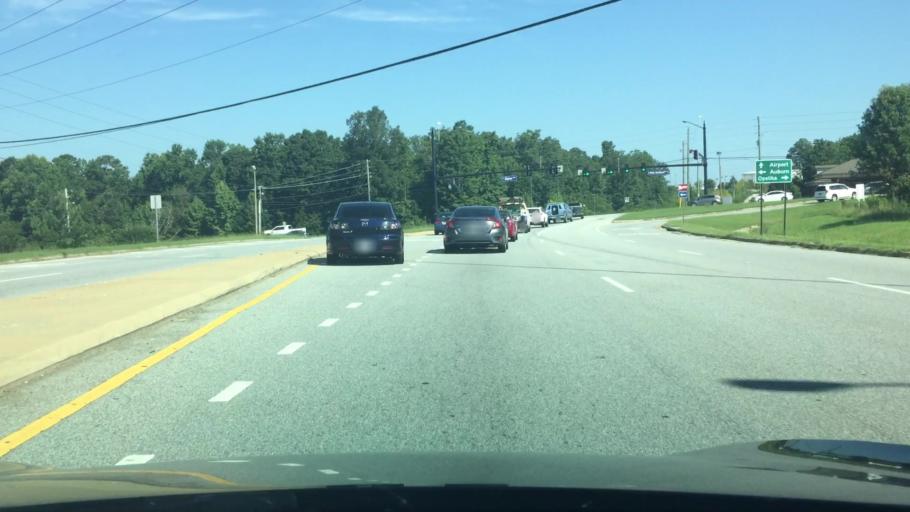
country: US
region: Alabama
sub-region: Lee County
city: Auburn
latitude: 32.6080
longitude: -85.4303
